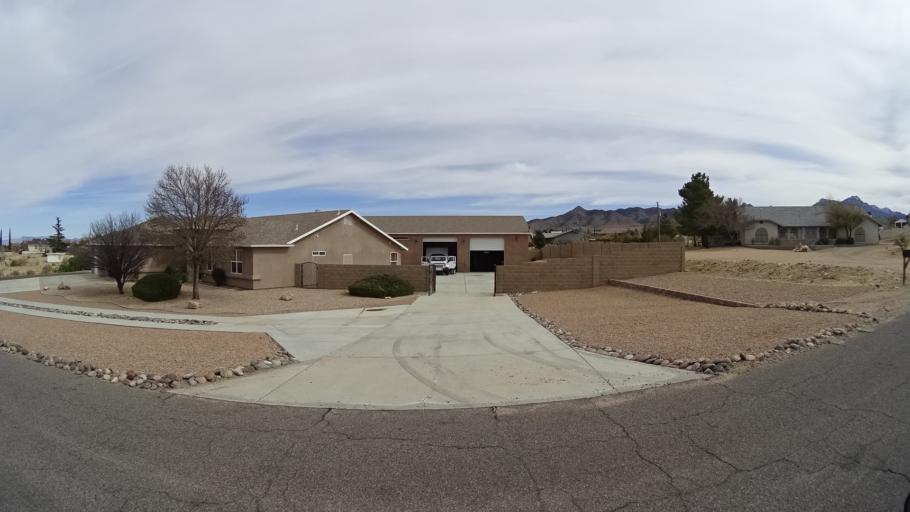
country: US
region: Arizona
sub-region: Mohave County
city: Kingman
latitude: 35.1877
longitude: -113.9928
